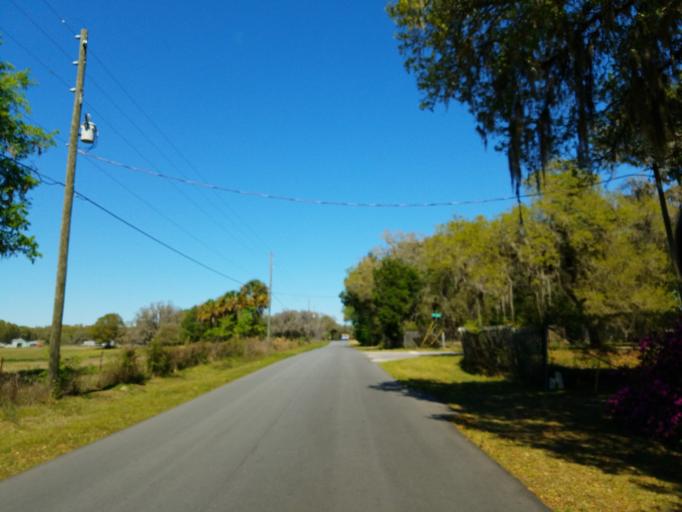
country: US
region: Florida
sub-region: Sumter County
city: Wildwood
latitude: 28.8024
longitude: -82.0489
